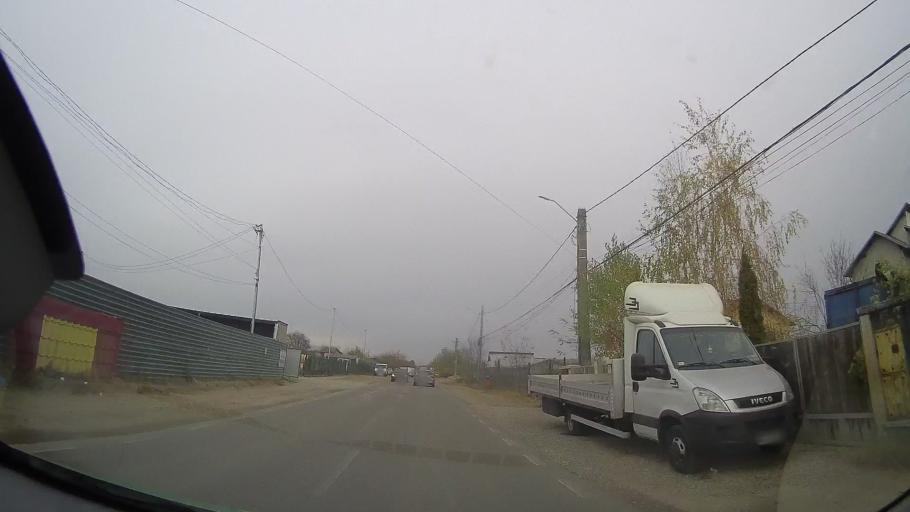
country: RO
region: Prahova
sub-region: Oras Baicoi
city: Liliesti
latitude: 45.0253
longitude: 25.8863
